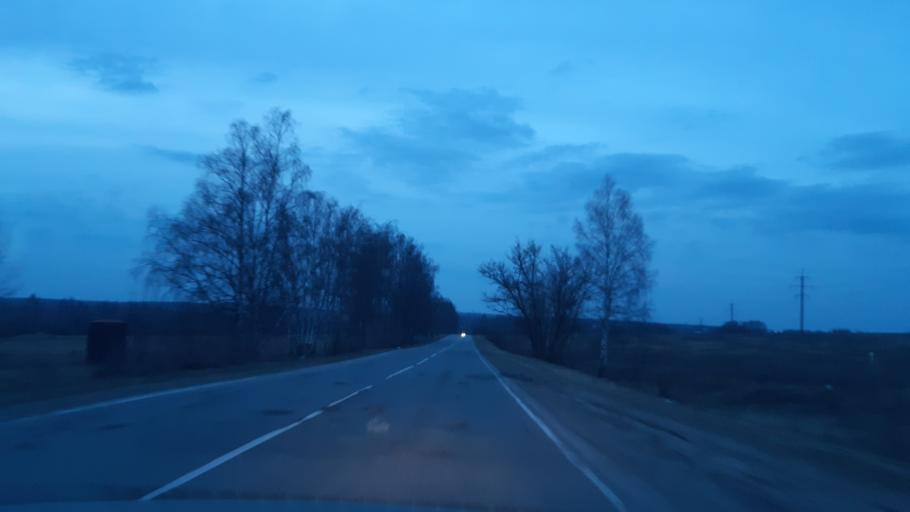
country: RU
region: Vladimir
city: Luknovo
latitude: 56.2014
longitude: 42.0335
